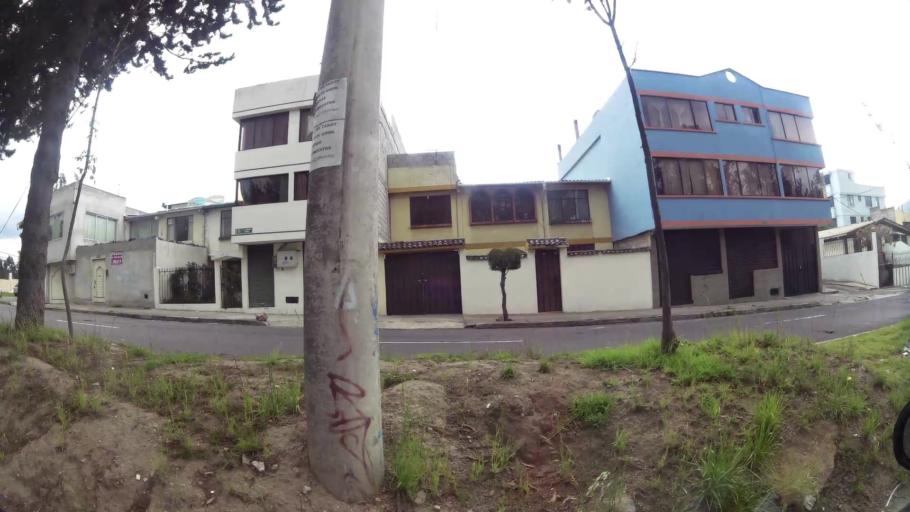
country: EC
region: Pichincha
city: Quito
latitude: -0.0910
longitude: -78.4673
